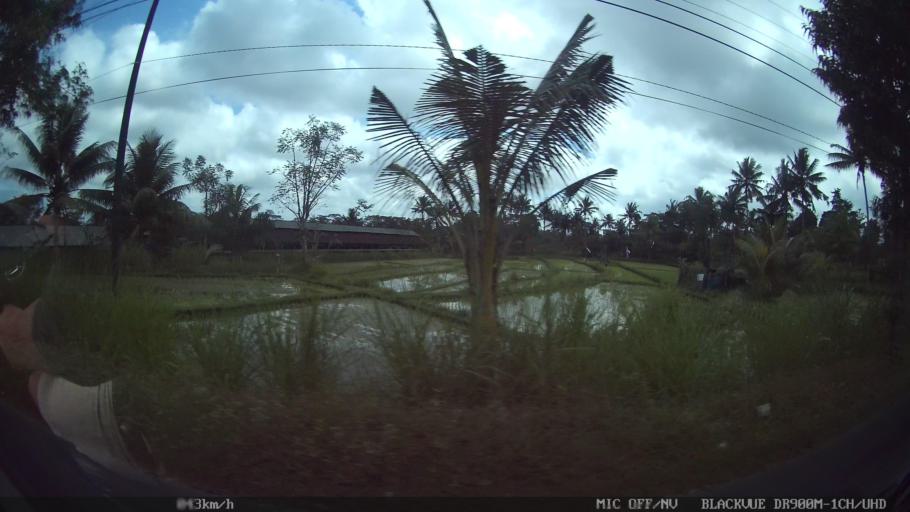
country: ID
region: Bali
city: Banjar Madangan Kaja
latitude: -8.4834
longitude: 115.3212
